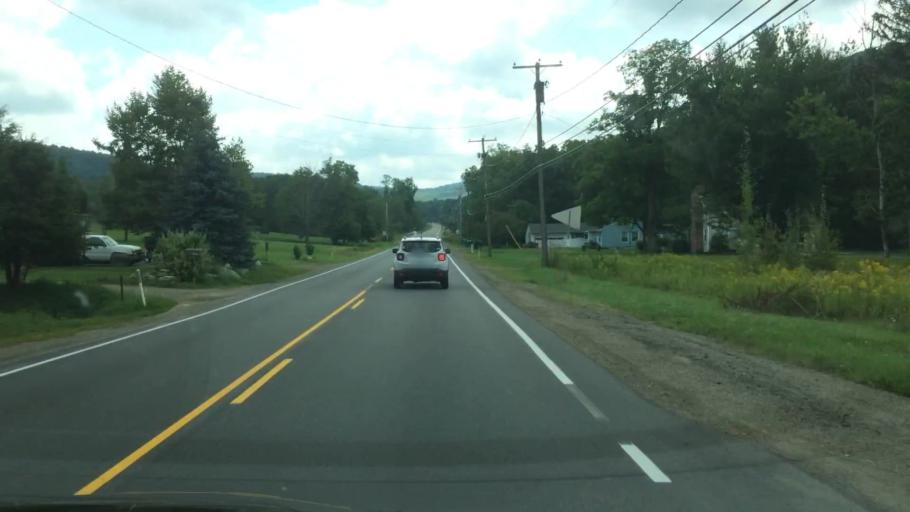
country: US
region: Pennsylvania
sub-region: McKean County
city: Bradford
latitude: 41.9009
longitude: -78.6109
